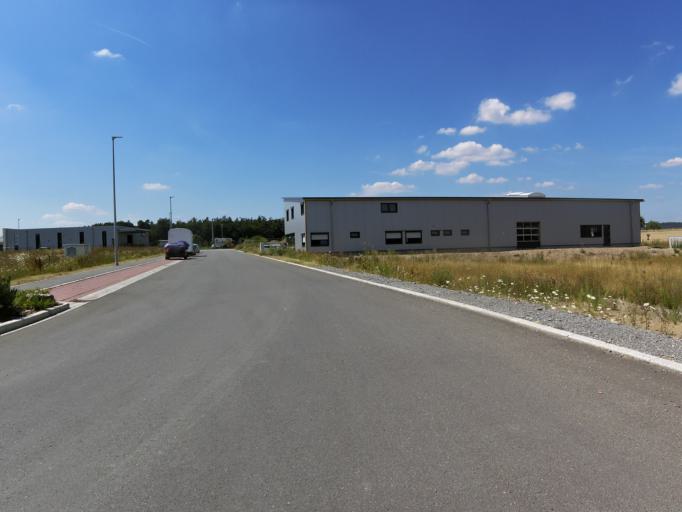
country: DE
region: Bavaria
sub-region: Regierungsbezirk Unterfranken
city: Gadheim
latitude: 49.8351
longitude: 9.9079
